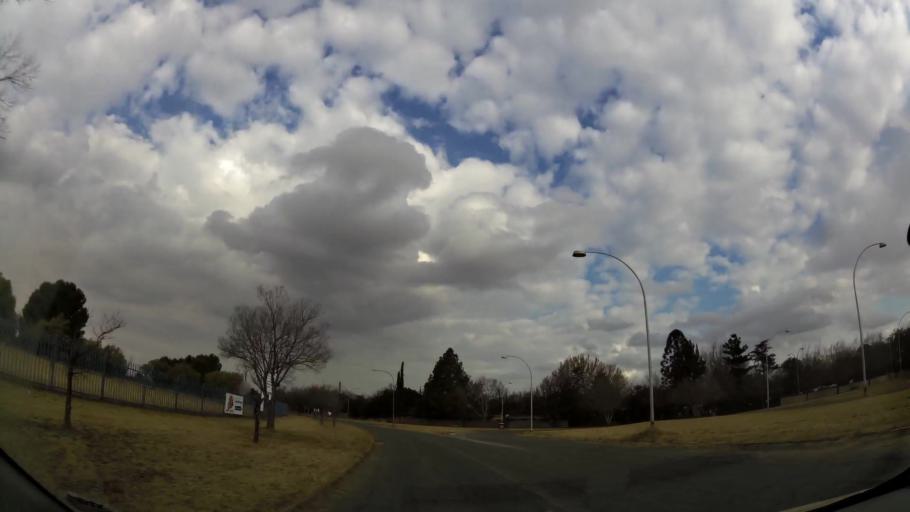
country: ZA
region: Orange Free State
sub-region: Fezile Dabi District Municipality
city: Sasolburg
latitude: -26.7955
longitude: 27.8247
